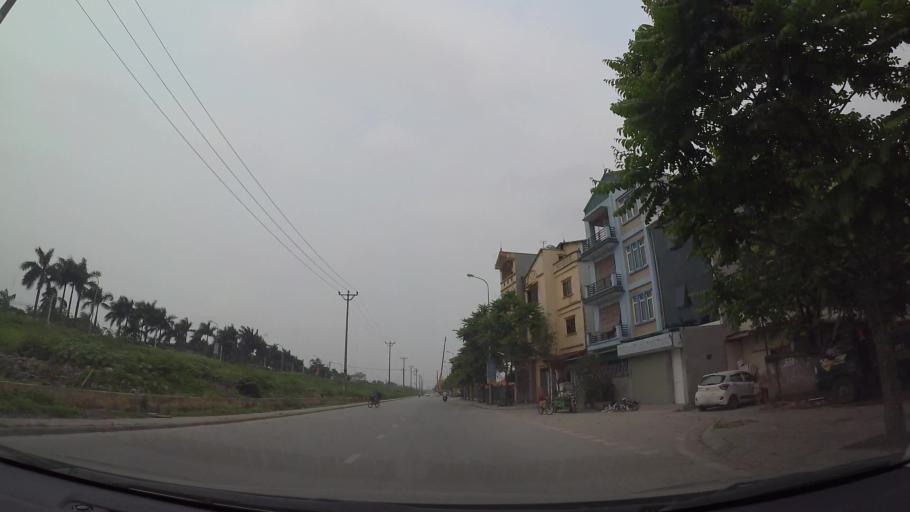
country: VN
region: Ha Noi
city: Hoan Kiem
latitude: 21.0705
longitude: 105.8825
